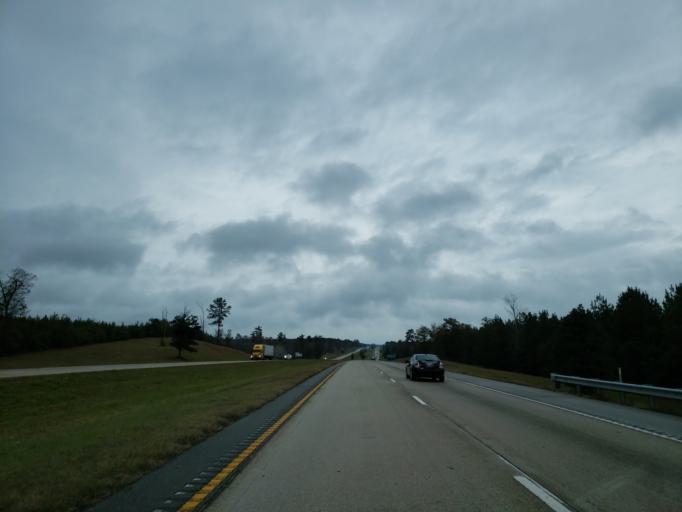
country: US
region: Mississippi
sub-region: Forrest County
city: Glendale
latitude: 31.4449
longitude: -89.3209
